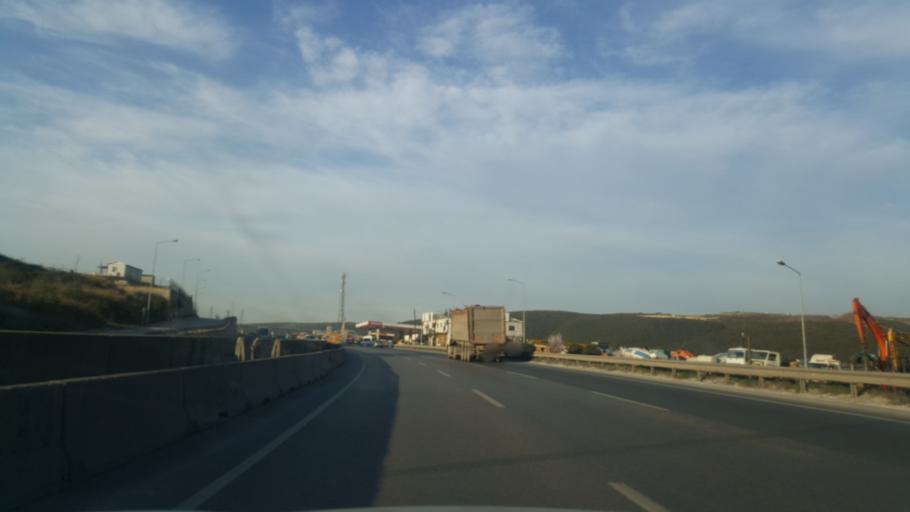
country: TR
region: Kocaeli
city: Tavsanli
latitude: 40.8014
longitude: 29.5270
